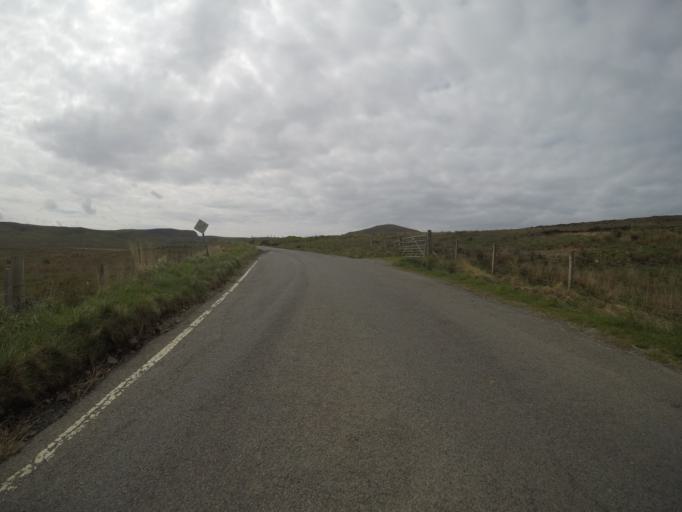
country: GB
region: Scotland
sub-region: Highland
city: Portree
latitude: 57.6829
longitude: -6.3213
